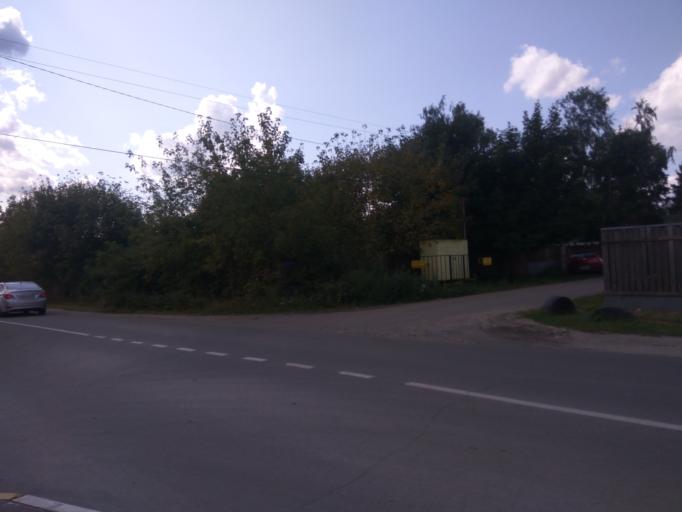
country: RU
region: Moskovskaya
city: Ramenskoye
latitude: 55.5631
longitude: 38.2187
